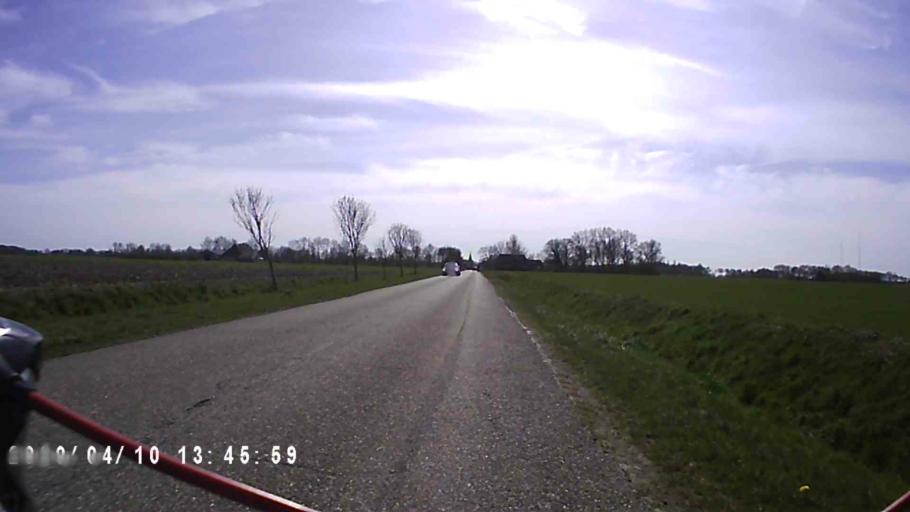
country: NL
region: Groningen
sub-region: Gemeente De Marne
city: Ulrum
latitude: 53.3721
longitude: 6.3723
